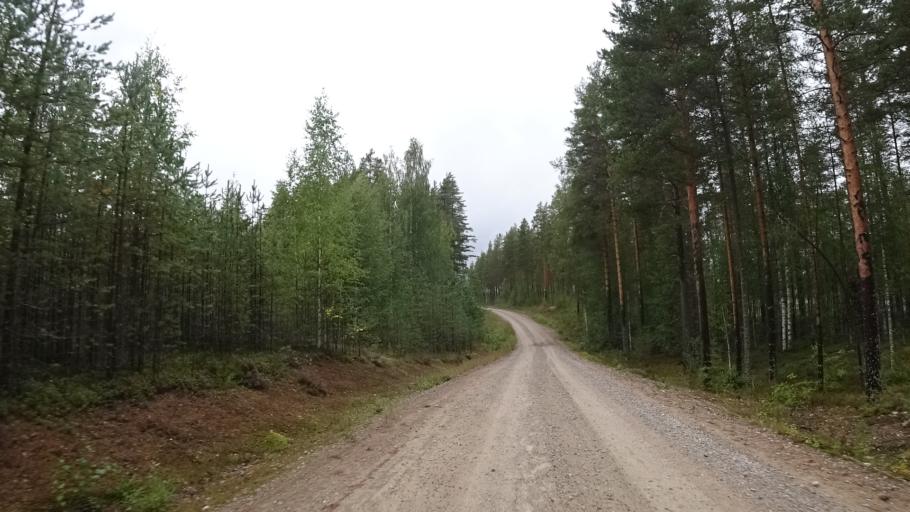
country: FI
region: North Karelia
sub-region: Pielisen Karjala
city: Lieksa
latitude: 63.5300
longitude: 30.0660
